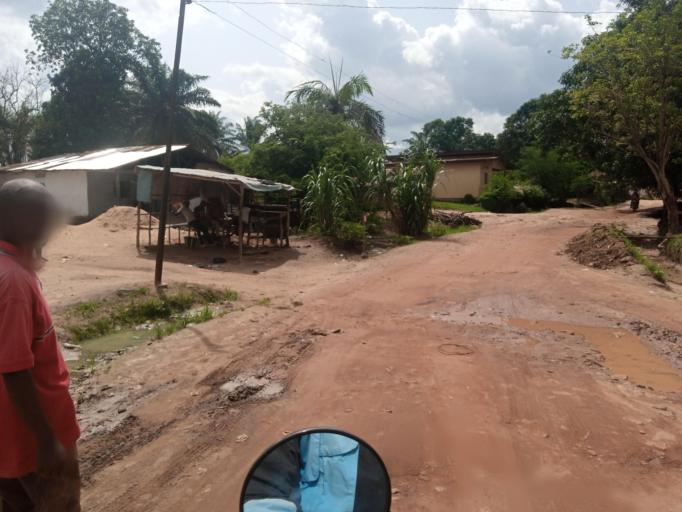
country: SL
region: Southern Province
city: Bo
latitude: 7.9776
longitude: -11.7318
